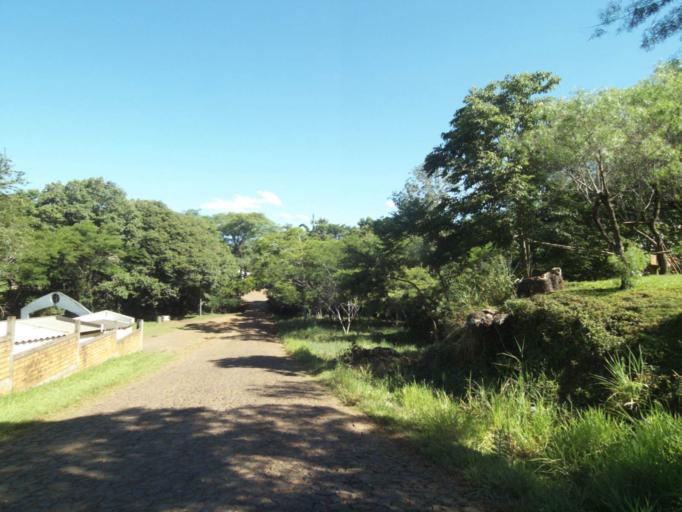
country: BR
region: Parana
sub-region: Ampere
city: Ampere
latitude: -26.1674
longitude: -53.3661
